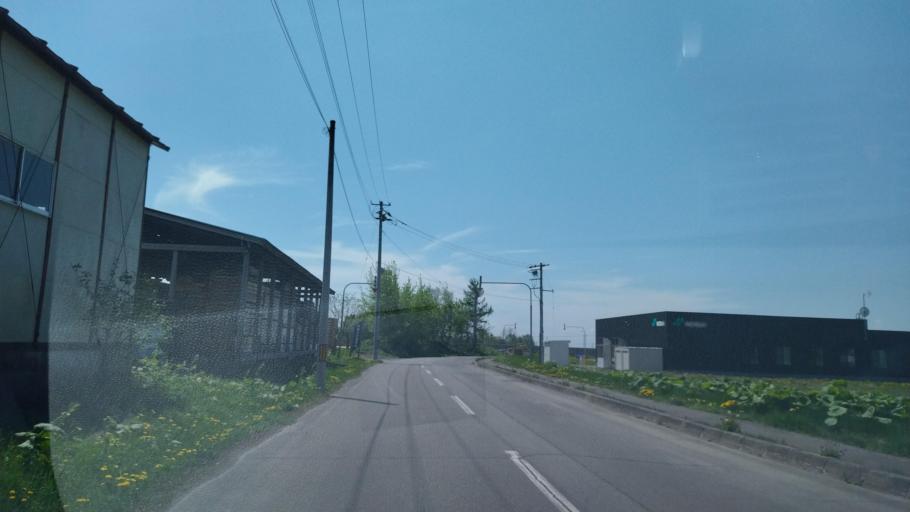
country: JP
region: Hokkaido
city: Otofuke
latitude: 43.2287
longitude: 143.2872
